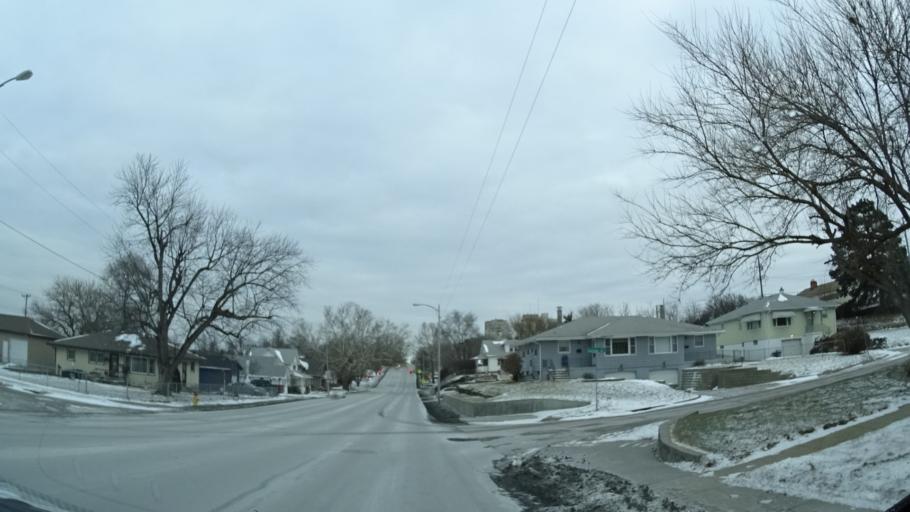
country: US
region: Nebraska
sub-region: Douglas County
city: Omaha
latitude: 41.2368
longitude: -95.9758
